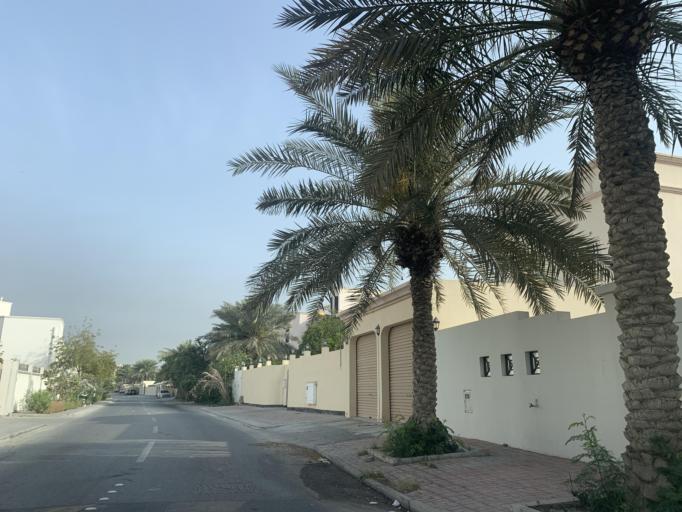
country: BH
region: Northern
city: Madinat `Isa
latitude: 26.1925
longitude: 50.5607
